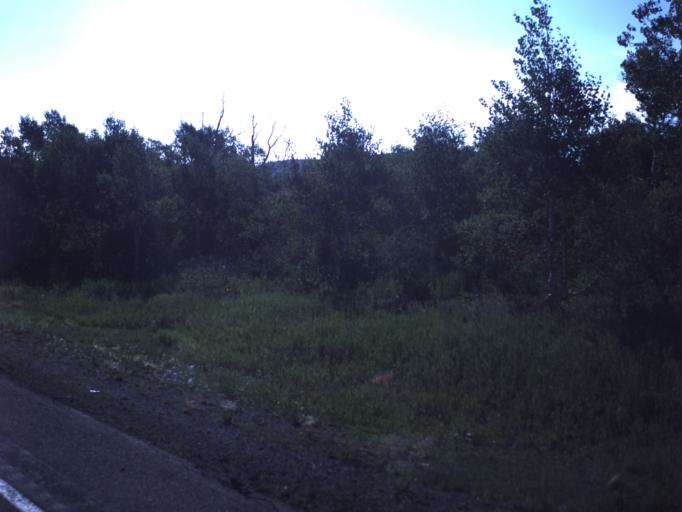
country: US
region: Utah
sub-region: Sanpete County
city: Fairview
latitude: 39.6717
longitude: -111.3220
